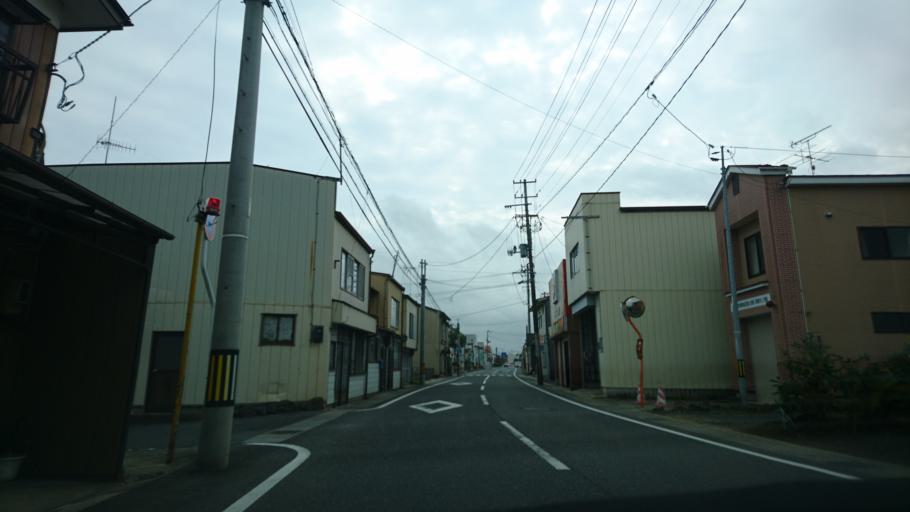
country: JP
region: Iwate
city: Ichinoseki
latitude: 38.7744
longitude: 141.1277
